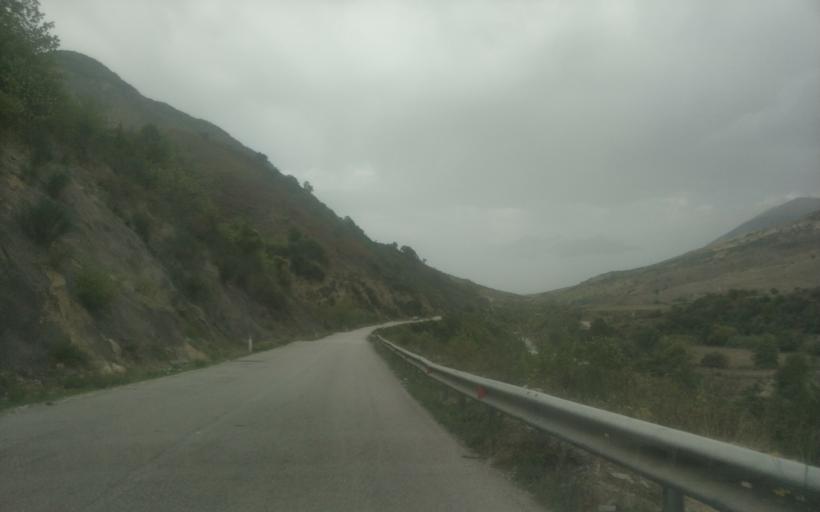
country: AL
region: Gjirokaster
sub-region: Rrethi i Gjirokastres
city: Picar
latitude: 40.2295
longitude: 20.0845
